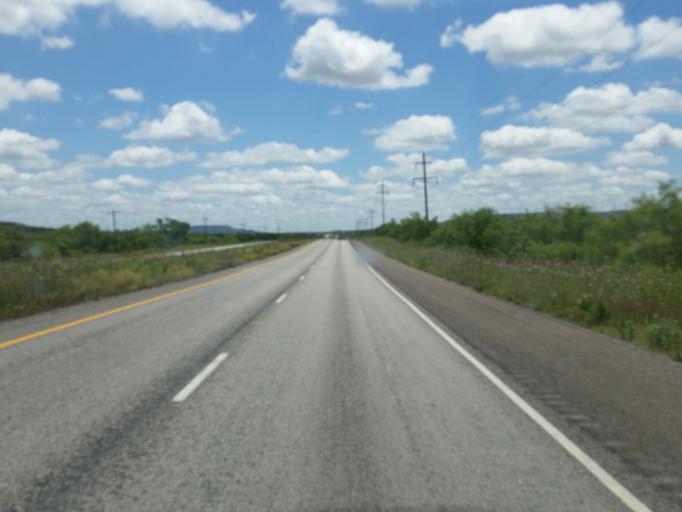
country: US
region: Texas
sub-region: Garza County
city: Post
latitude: 32.9994
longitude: -101.1574
